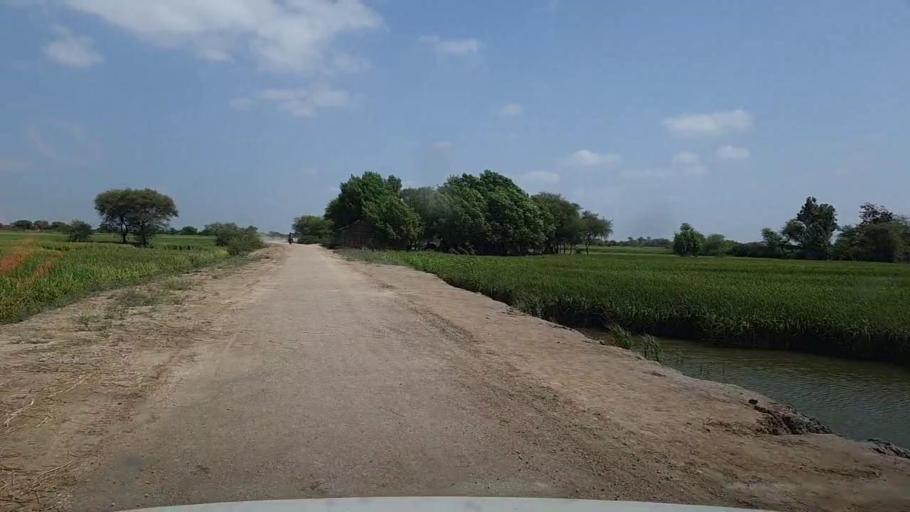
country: PK
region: Sindh
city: Kario
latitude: 24.6885
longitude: 68.5881
